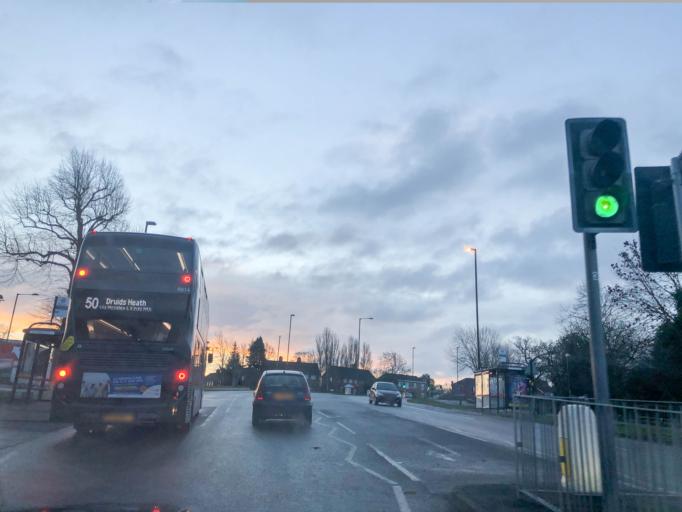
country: GB
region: England
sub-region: Solihull
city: Tidbury Green
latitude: 52.4144
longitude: -1.8856
